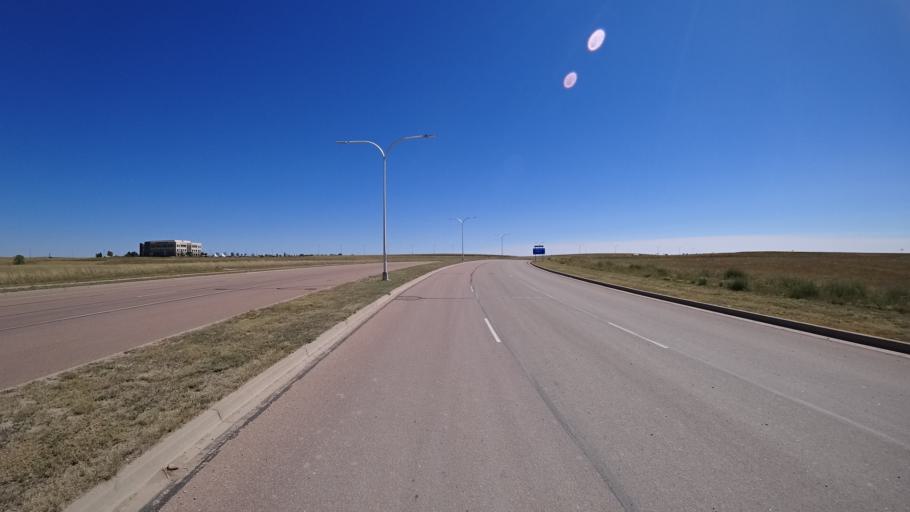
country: US
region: Colorado
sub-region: El Paso County
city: Security-Widefield
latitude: 38.7770
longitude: -104.7064
